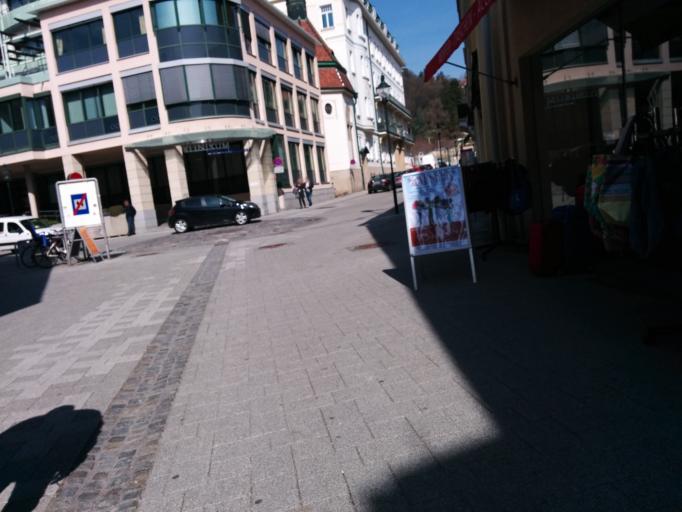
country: AT
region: Lower Austria
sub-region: Politischer Bezirk Baden
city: Baden
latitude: 48.0089
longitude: 16.2338
